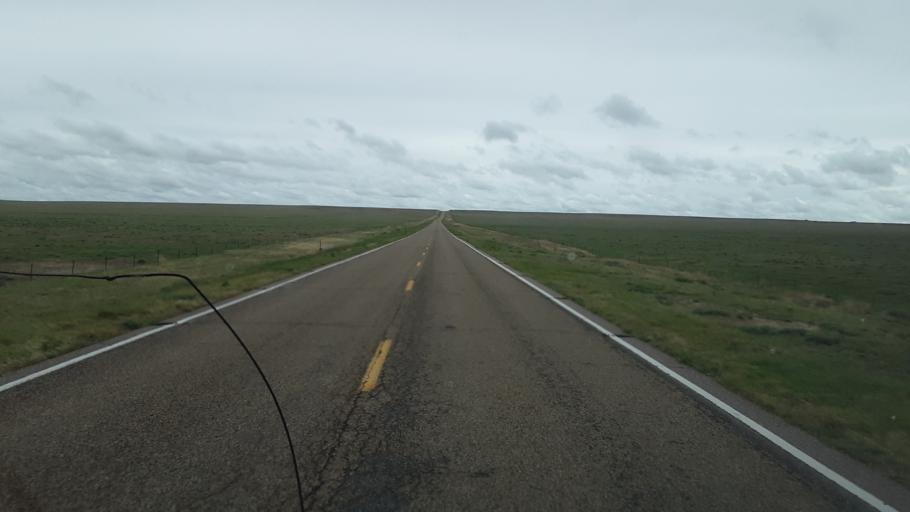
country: US
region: Colorado
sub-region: Lincoln County
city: Hugo
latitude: 38.8498
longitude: -103.3746
